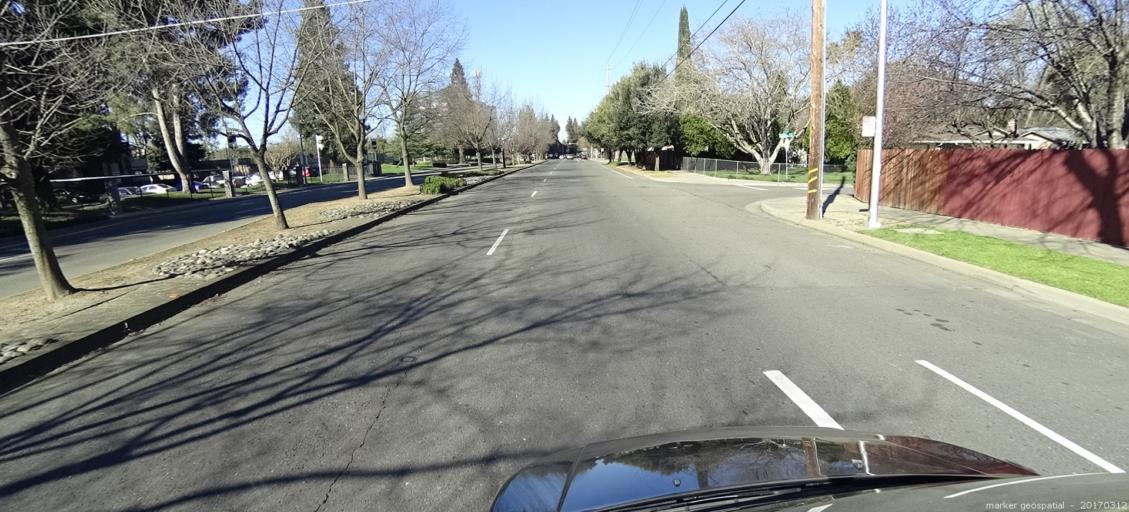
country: US
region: California
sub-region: Sacramento County
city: Sacramento
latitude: 38.6128
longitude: -121.5020
